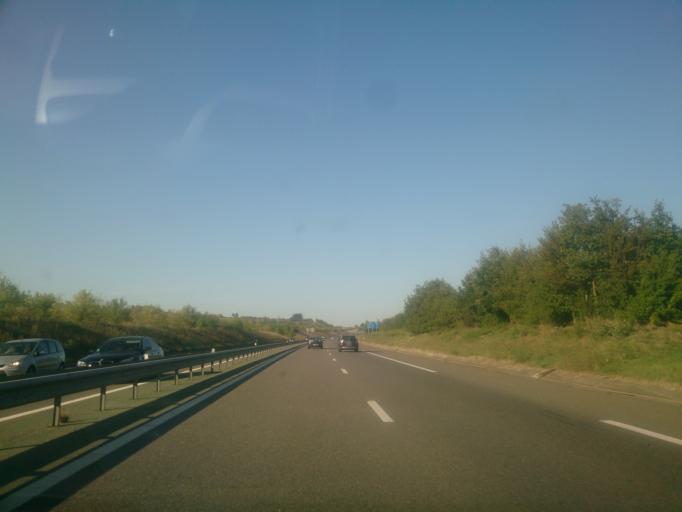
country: FR
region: Midi-Pyrenees
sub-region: Departement du Tarn-et-Garonne
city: Caussade
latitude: 44.1609
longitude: 1.5194
